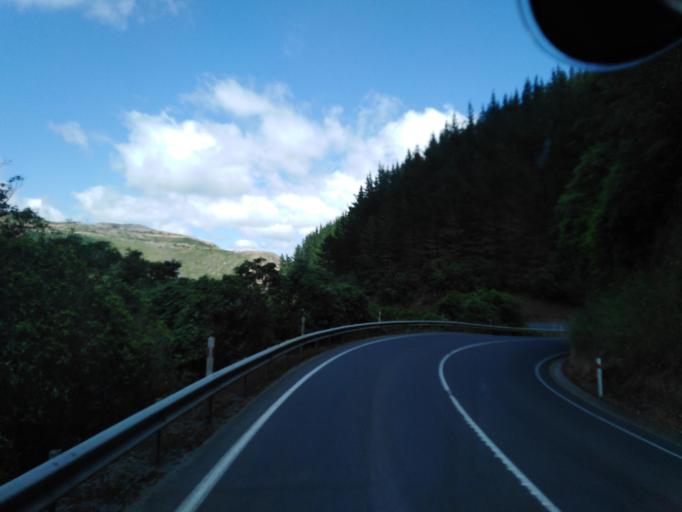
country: NZ
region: Nelson
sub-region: Nelson City
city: Nelson
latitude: -41.2268
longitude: 173.4184
